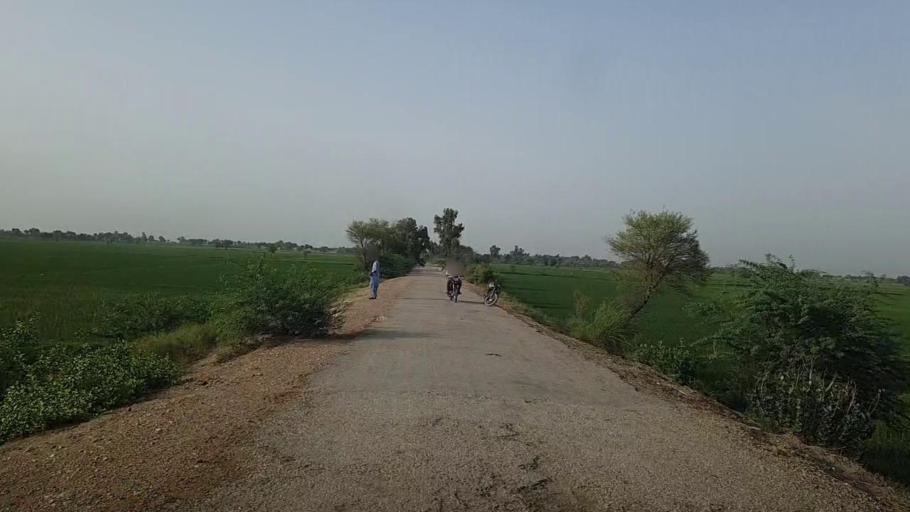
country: PK
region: Sindh
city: Mehar
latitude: 27.1270
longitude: 67.7891
